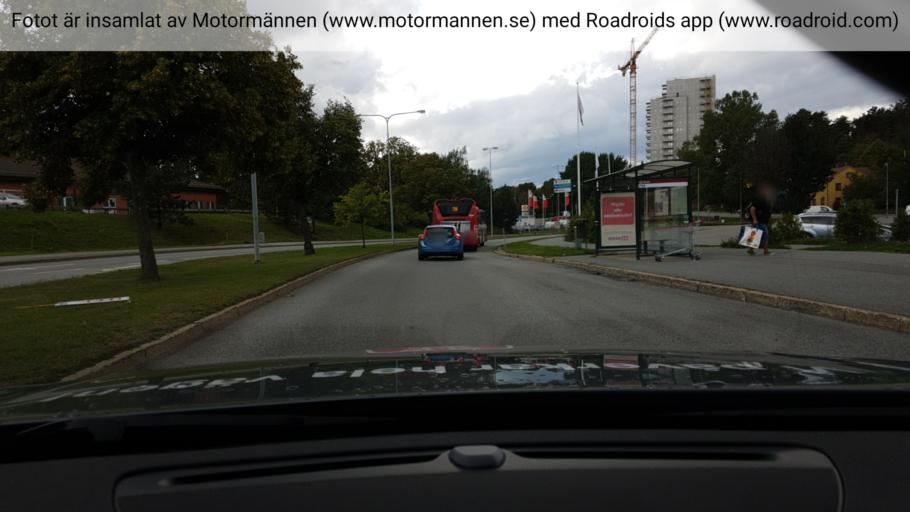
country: SE
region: Stockholm
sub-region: Sodertalje Kommun
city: Soedertaelje
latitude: 59.2055
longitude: 17.6453
